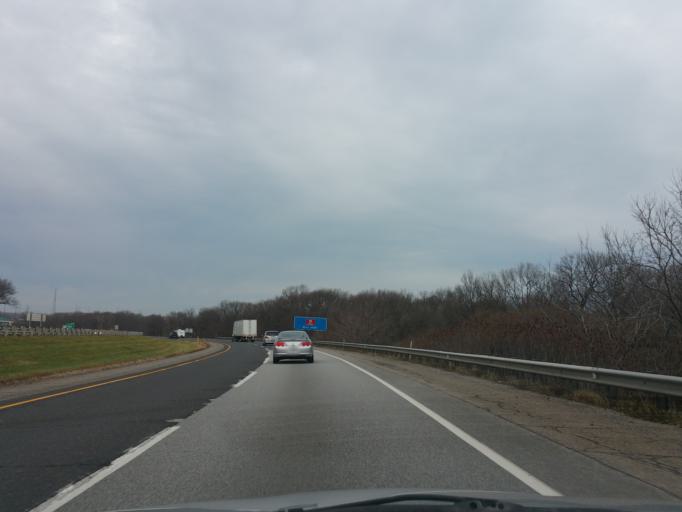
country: US
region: Indiana
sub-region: Porter County
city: Portage
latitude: 41.5853
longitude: -87.2027
